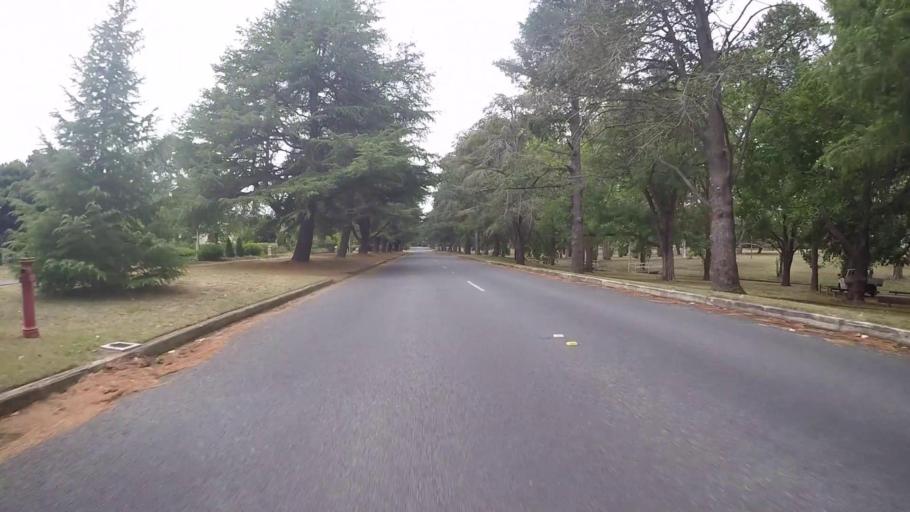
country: AU
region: Australian Capital Territory
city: Forrest
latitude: -35.3130
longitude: 149.1382
